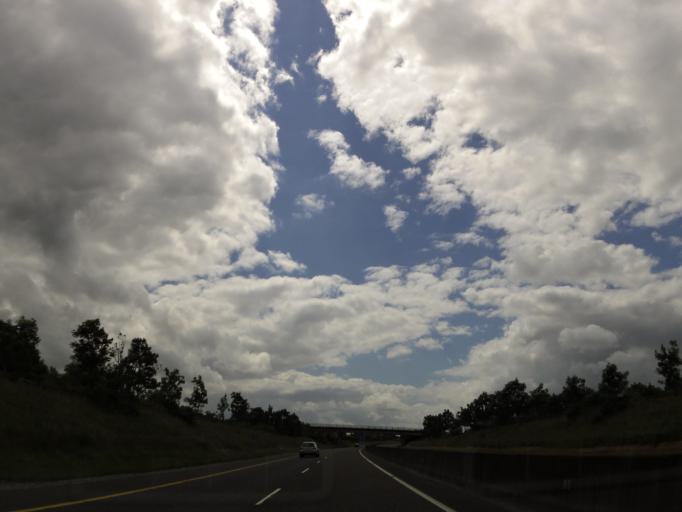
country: IE
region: Munster
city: Cashel
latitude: 52.5250
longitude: -7.8584
